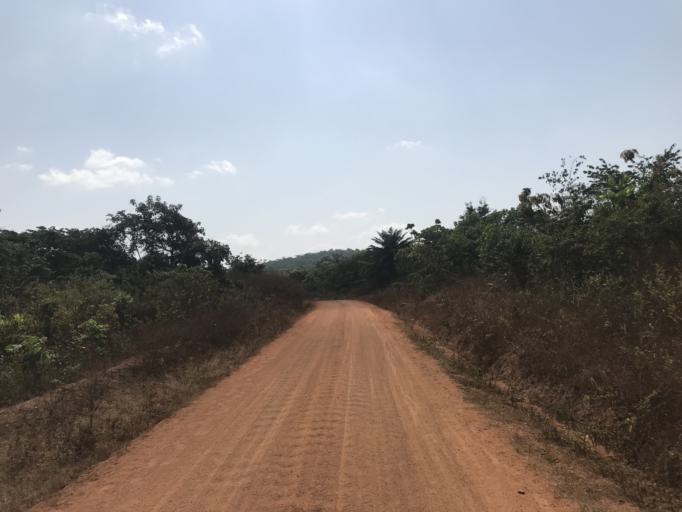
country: NG
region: Osun
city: Ifon
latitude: 7.8990
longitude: 4.4772
